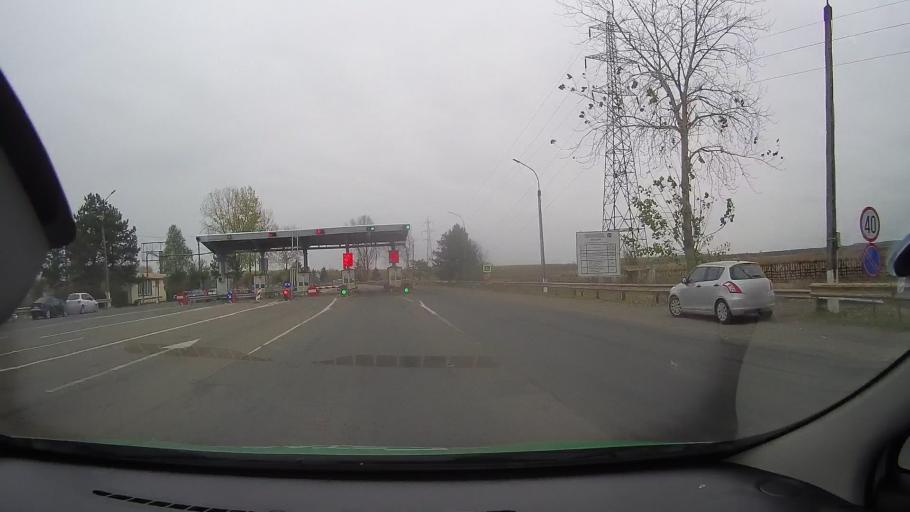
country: RO
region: Ialomita
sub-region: Comuna Giurgeni
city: Giurgeni
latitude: 44.7491
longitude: 27.8931
